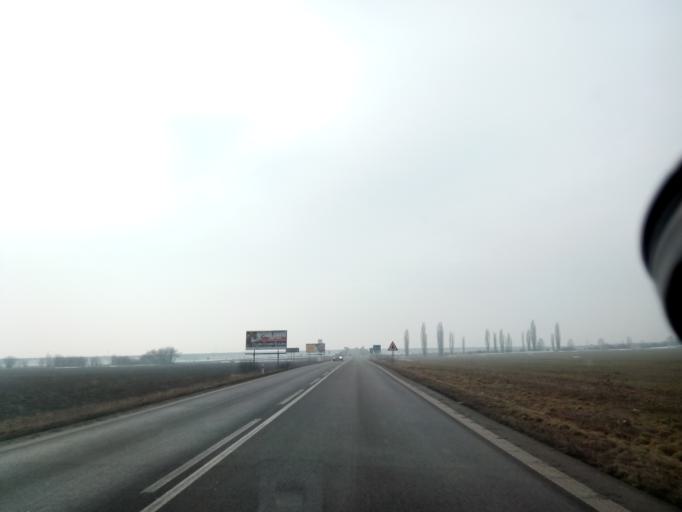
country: SK
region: Kosicky
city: Kosice
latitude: 48.6482
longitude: 21.2693
